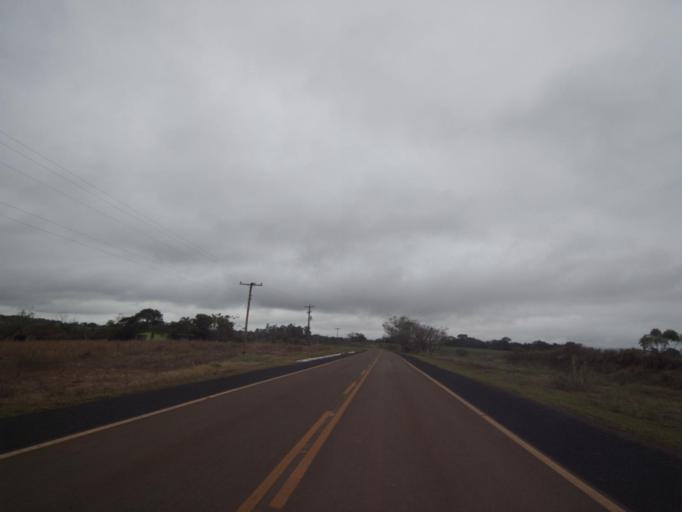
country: AR
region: Misiones
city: El Soberbio
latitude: -27.2953
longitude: -54.1748
